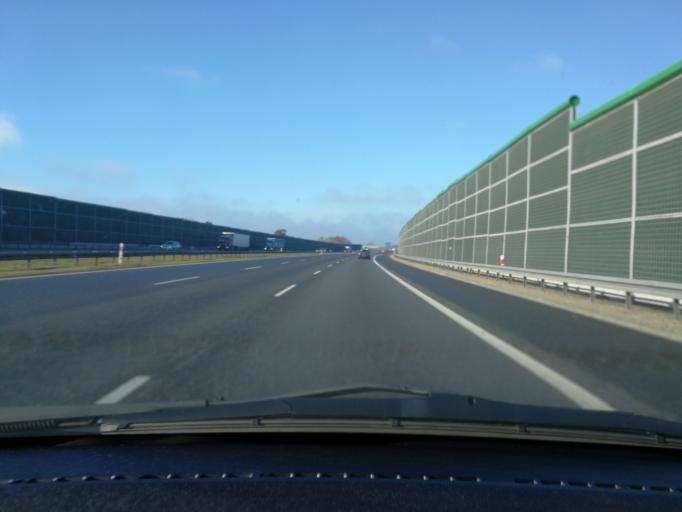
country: PL
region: Masovian Voivodeship
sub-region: Powiat pruszkowski
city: Pruszkow
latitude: 52.1928
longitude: 20.8139
